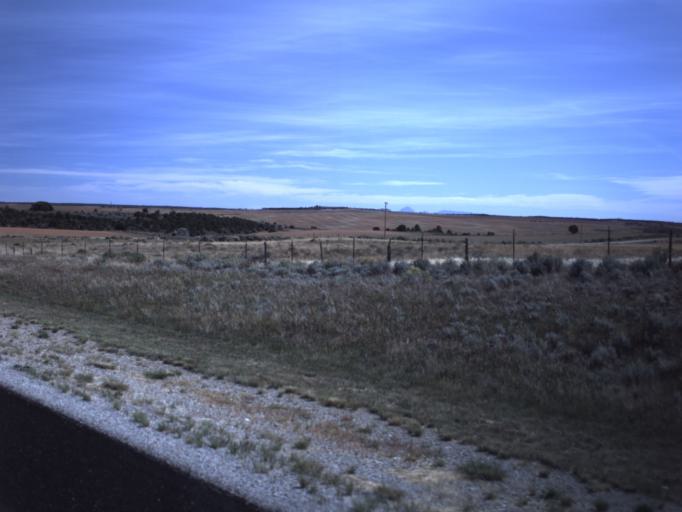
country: US
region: Utah
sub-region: San Juan County
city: Monticello
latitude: 37.8648
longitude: -109.2286
